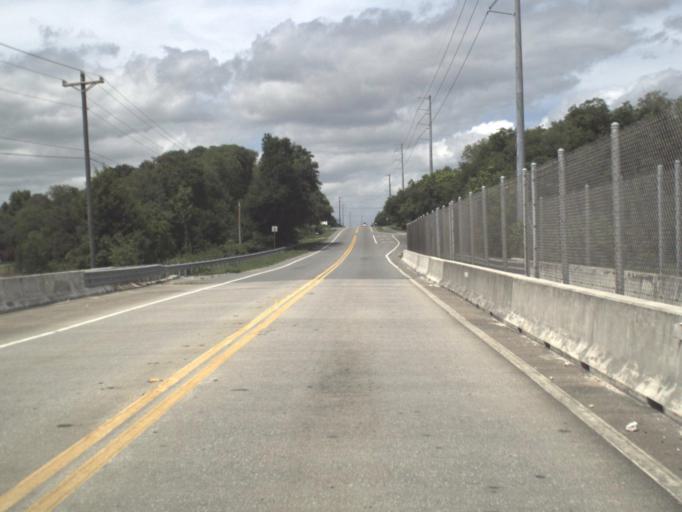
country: US
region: Florida
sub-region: Clay County
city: Keystone Heights
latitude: 29.7963
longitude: -82.0224
